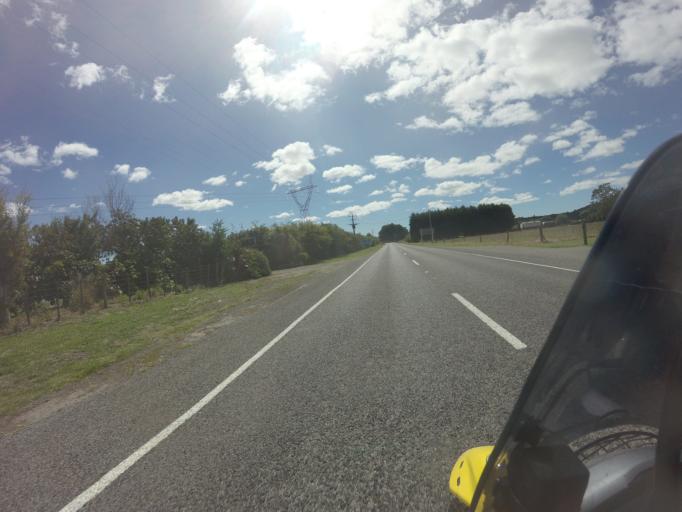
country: NZ
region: Bay of Plenty
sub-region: Whakatane District
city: Edgecumbe
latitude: -38.0736
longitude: 176.8179
